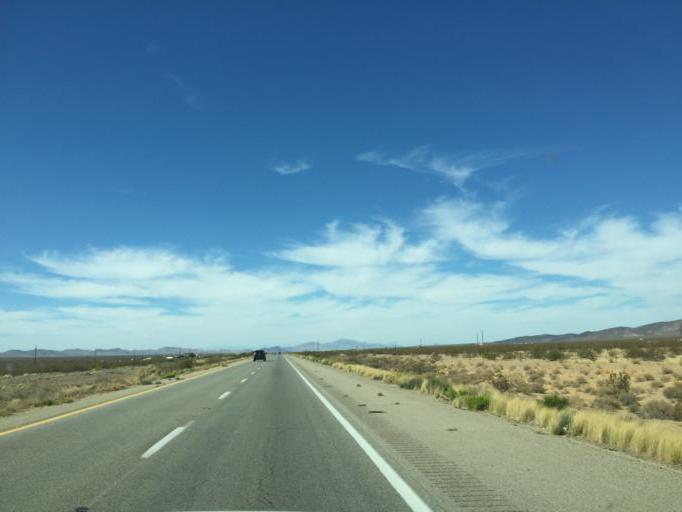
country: US
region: Arizona
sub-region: Mohave County
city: Dolan Springs
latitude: 35.5862
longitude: -114.3914
